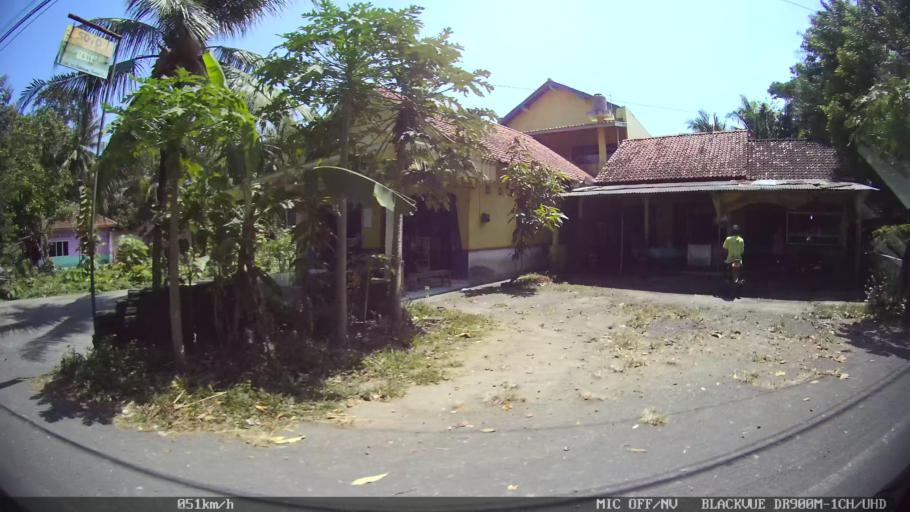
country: ID
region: Daerah Istimewa Yogyakarta
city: Srandakan
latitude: -7.9438
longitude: 110.2288
